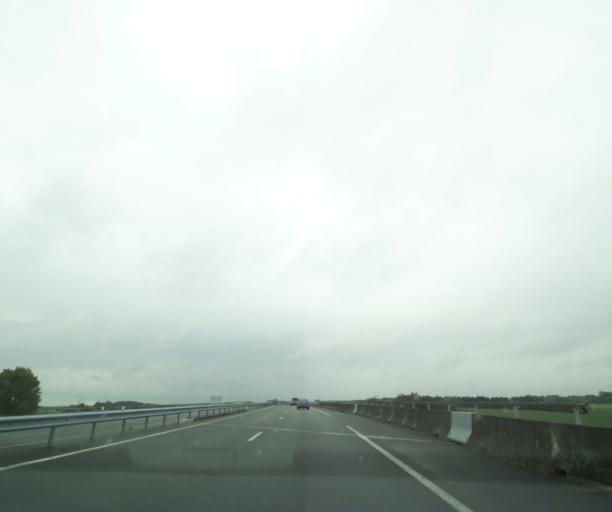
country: FR
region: Poitou-Charentes
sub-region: Departement de la Charente-Maritime
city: Nieul-les-Saintes
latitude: 45.6995
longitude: -0.7475
